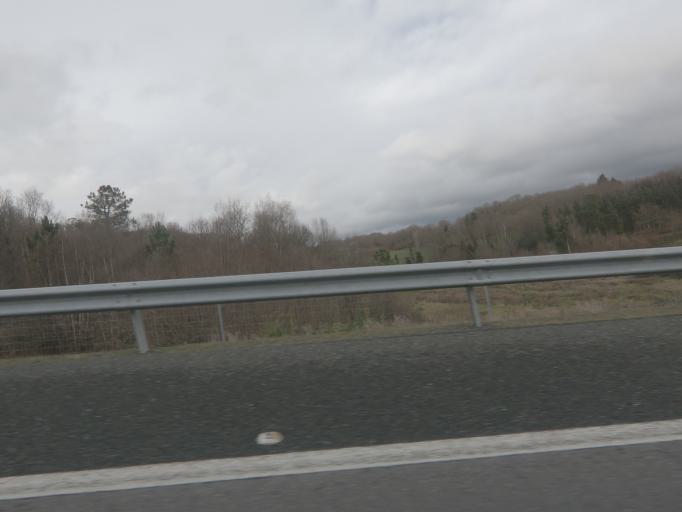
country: ES
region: Galicia
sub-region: Provincia de Pontevedra
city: Lalin
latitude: 42.6242
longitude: -8.1036
